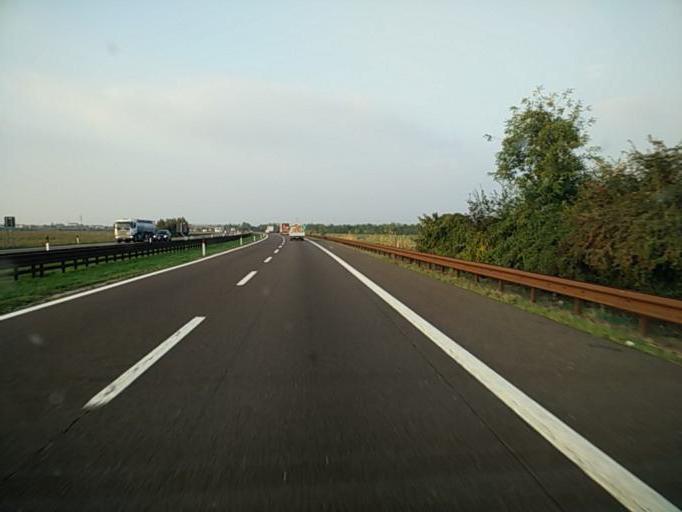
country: IT
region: Veneto
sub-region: Provincia di Verona
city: Alpo
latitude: 45.3581
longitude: 10.9206
